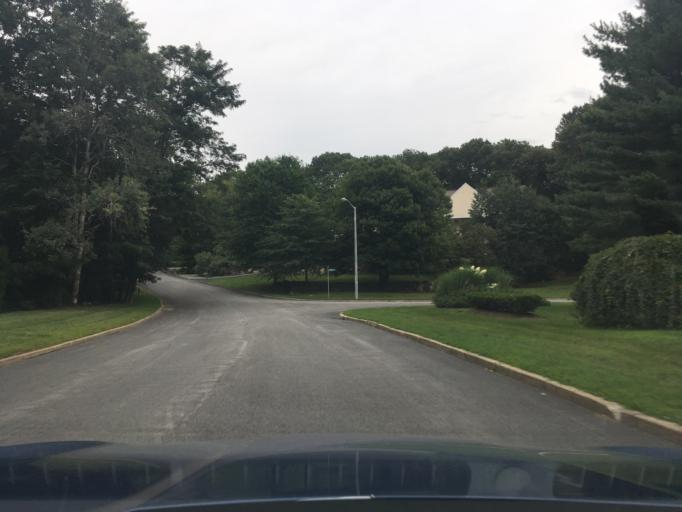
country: US
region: Rhode Island
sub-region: Kent County
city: East Greenwich
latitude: 41.6331
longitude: -71.5046
